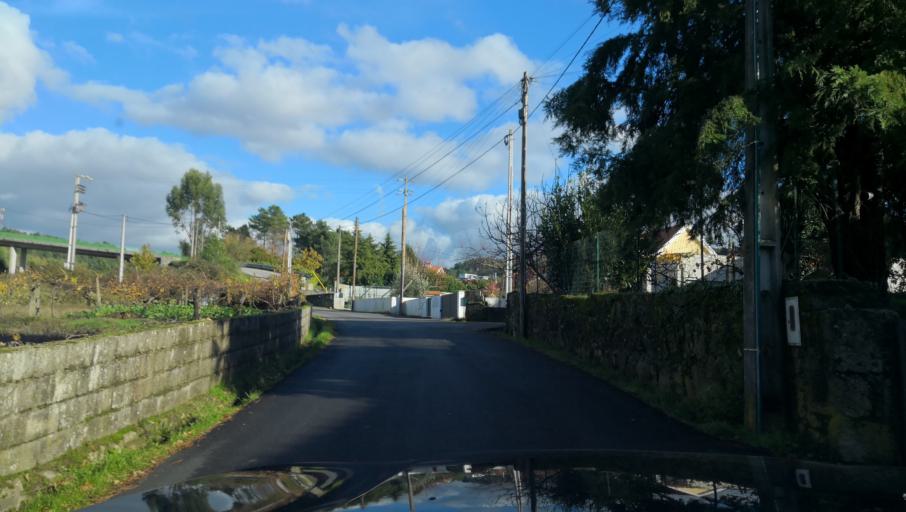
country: PT
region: Vila Real
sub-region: Vila Real
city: Vila Real
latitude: 41.3151
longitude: -7.7185
